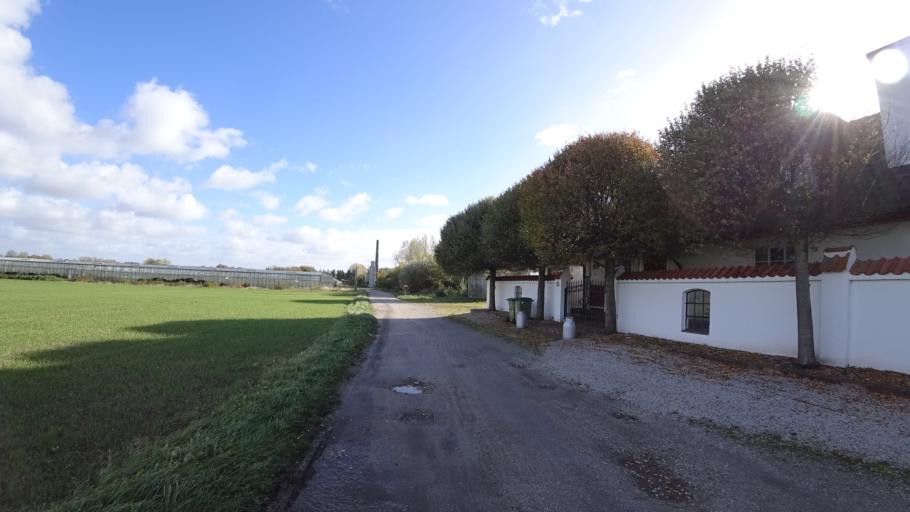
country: SE
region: Skane
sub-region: Staffanstorps Kommun
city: Hjaerup
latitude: 55.6846
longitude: 13.1646
